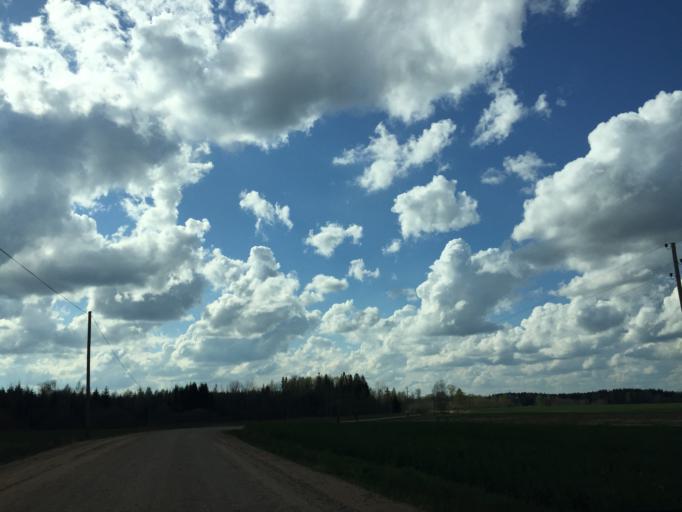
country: LV
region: Beverina
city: Murmuiza
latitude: 57.4734
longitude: 25.5151
